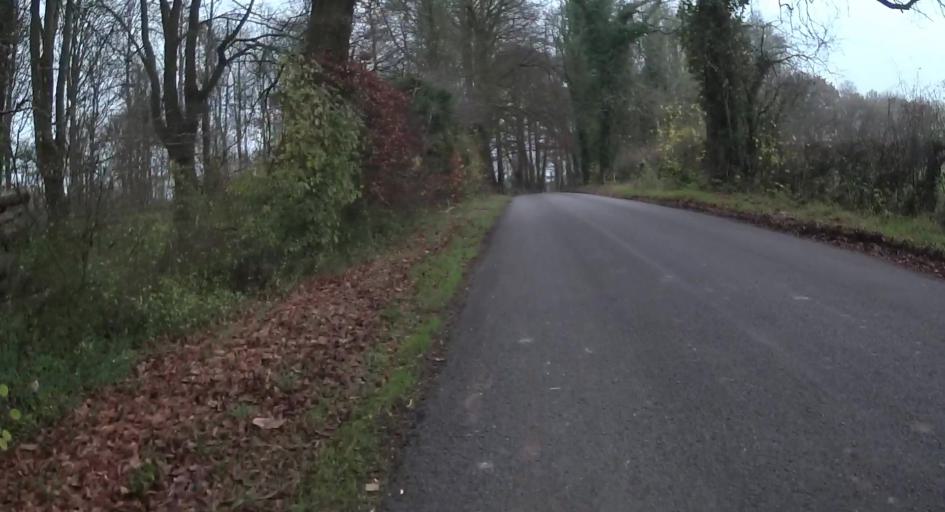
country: GB
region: England
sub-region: Hampshire
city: Kings Worthy
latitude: 51.1185
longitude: -1.2108
